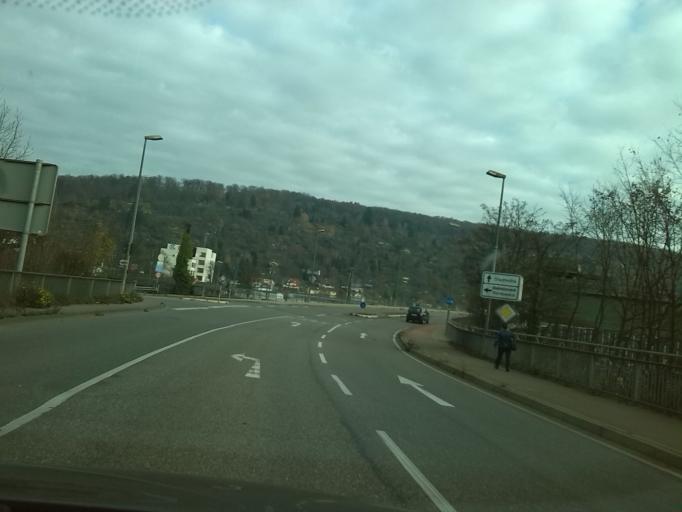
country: DE
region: Baden-Wuerttemberg
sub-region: Regierungsbezirk Stuttgart
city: Plochingen
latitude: 48.7138
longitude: 9.4073
